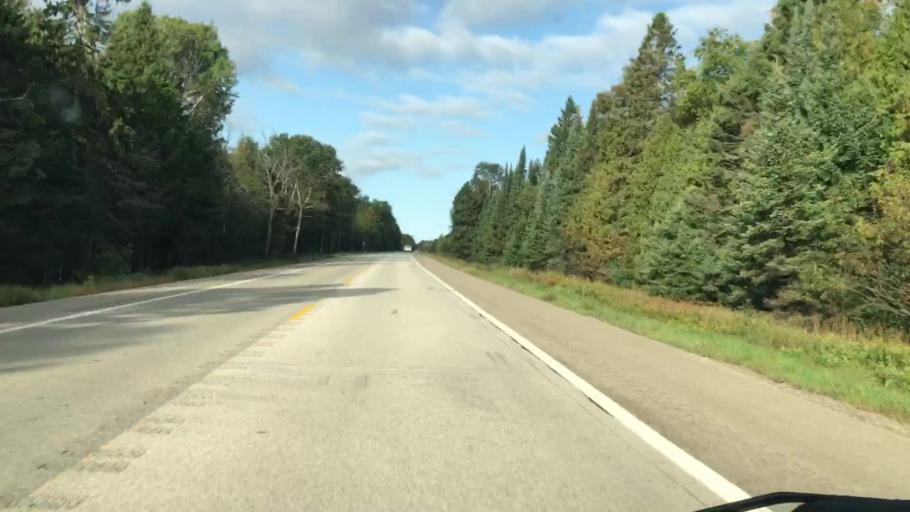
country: US
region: Michigan
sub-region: Luce County
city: Newberry
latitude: 46.3319
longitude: -85.0811
